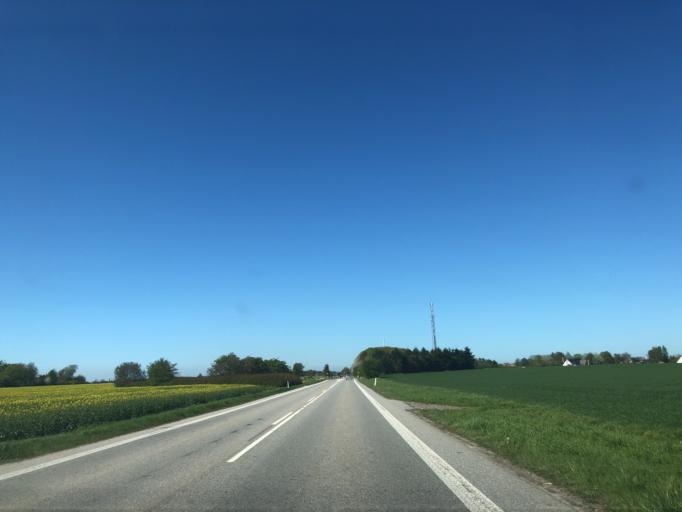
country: DK
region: Zealand
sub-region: Stevns Kommune
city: Store Heddinge
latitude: 55.3184
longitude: 12.3673
